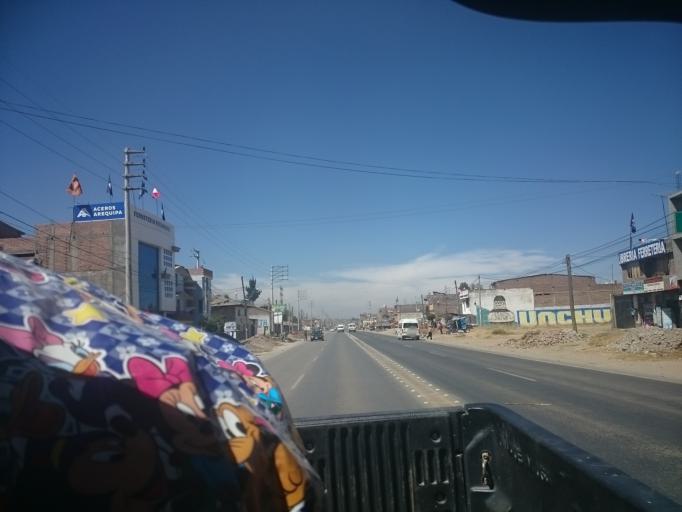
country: PE
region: Junin
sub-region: Provincia de Huancayo
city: San Agustin
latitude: -11.9935
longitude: -75.2561
